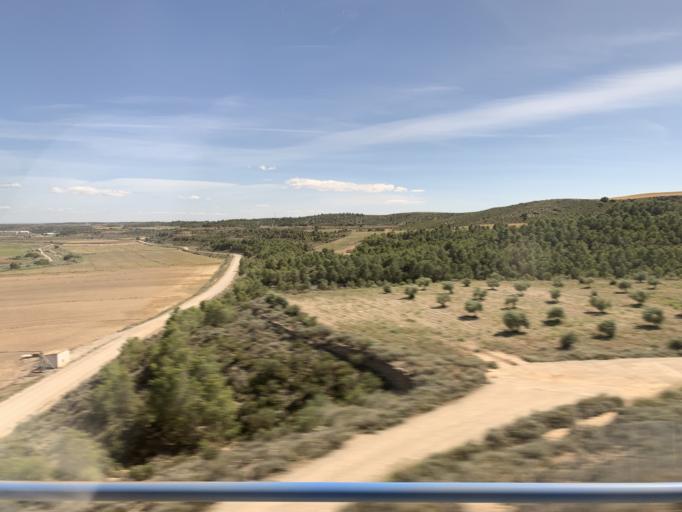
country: ES
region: Aragon
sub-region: Provincia de Huesca
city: Penalba
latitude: 41.5279
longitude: -0.0506
